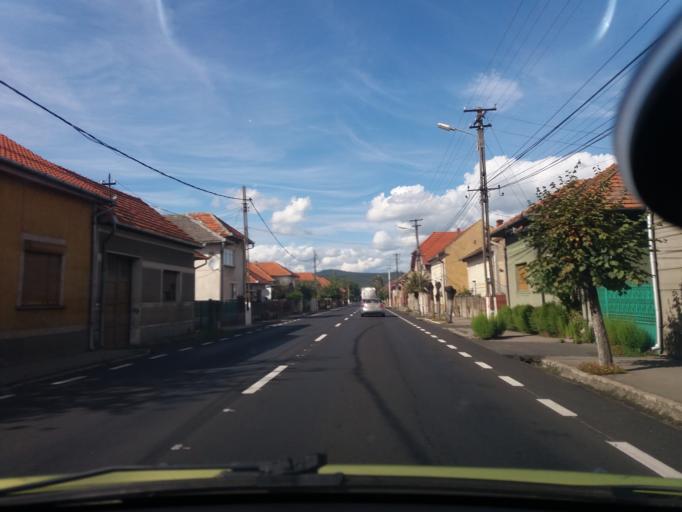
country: RO
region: Hunedoara
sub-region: Comuna Ilia
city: Ilia
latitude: 45.9366
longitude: 22.6511
